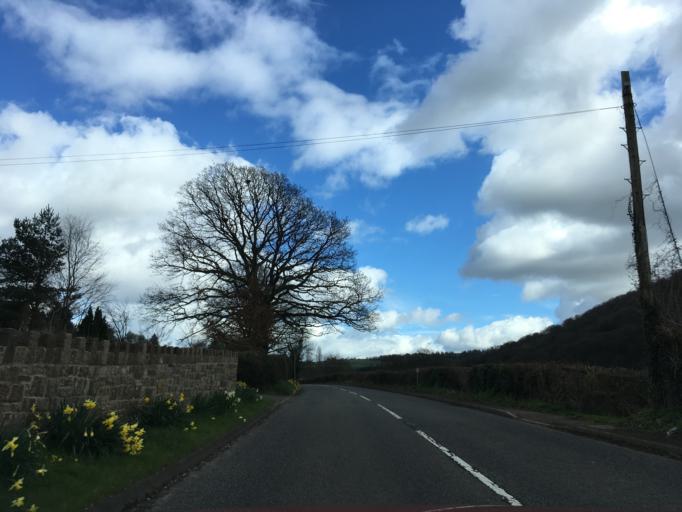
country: GB
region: Wales
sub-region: Monmouthshire
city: Tintern
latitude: 51.7355
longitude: -2.6819
